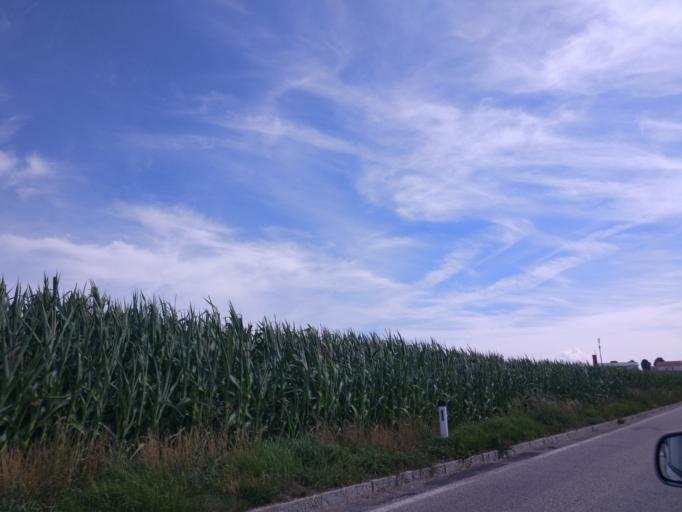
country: DE
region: Bavaria
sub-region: Upper Bavaria
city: Burghausen
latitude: 48.1517
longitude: 12.8397
